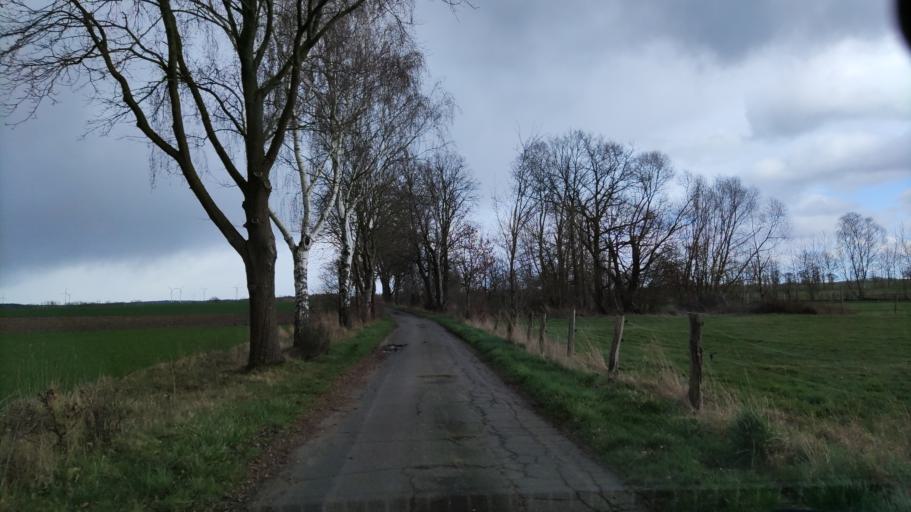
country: DE
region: Lower Saxony
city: Dahlenburg
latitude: 53.1953
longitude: 10.7045
